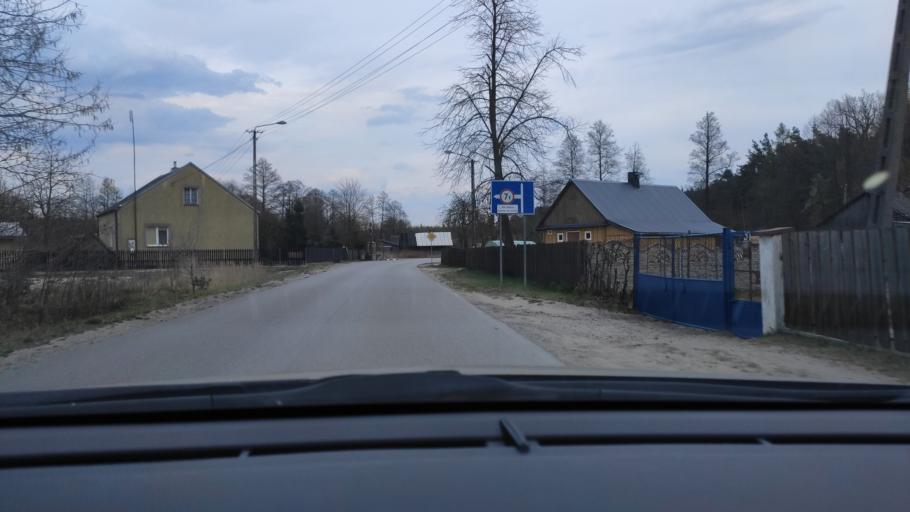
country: PL
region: Masovian Voivodeship
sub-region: Powiat radomski
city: Pionki
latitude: 51.5377
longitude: 21.4021
